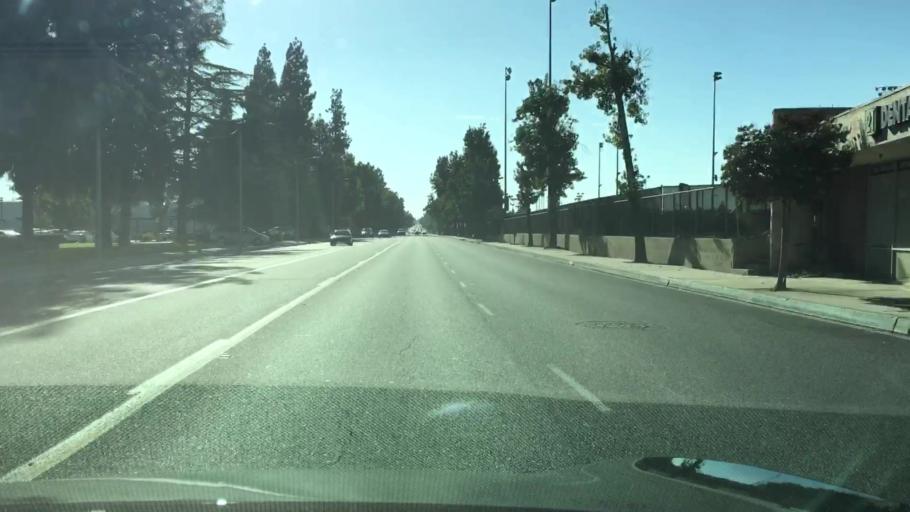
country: US
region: California
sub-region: Los Angeles County
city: Arcadia
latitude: 34.1294
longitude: -118.0321
